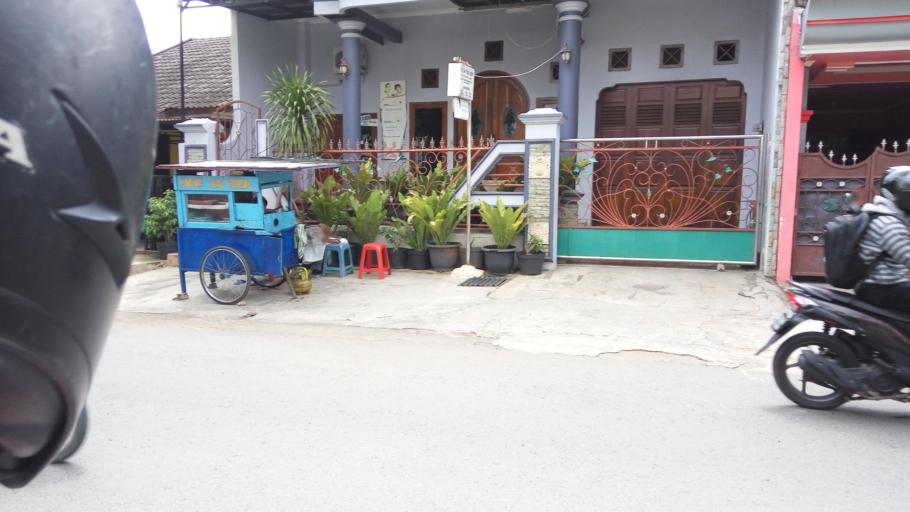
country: ID
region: Central Java
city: Mranggen
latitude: -7.0434
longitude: 110.4792
